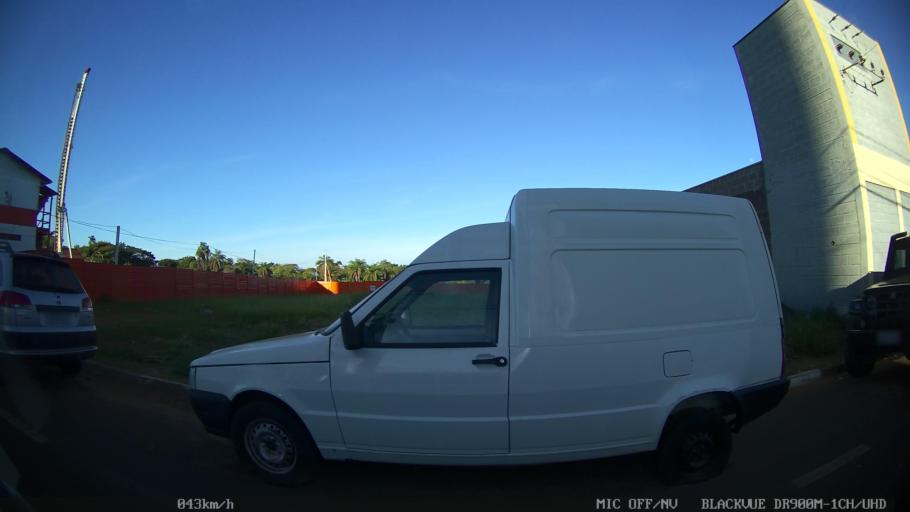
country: BR
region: Sao Paulo
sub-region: Franca
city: Franca
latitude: -20.5645
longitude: -47.4053
